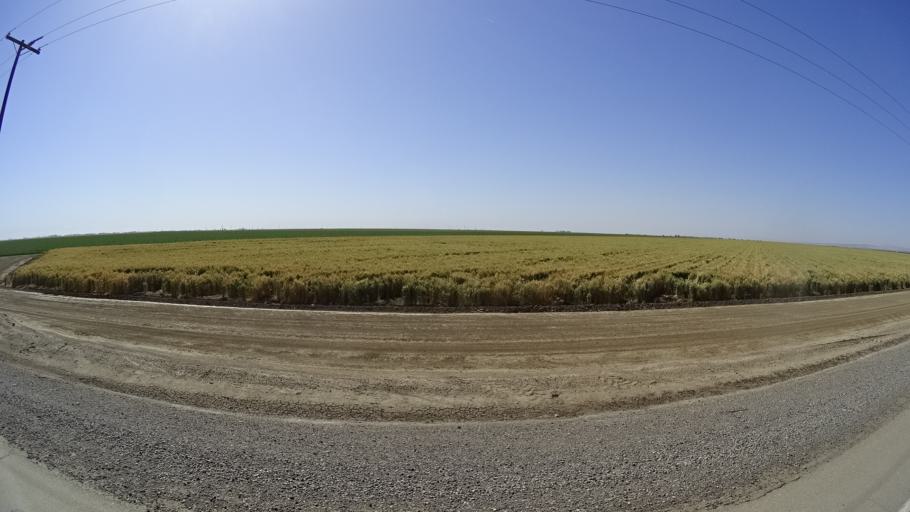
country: US
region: California
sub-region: Kings County
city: Lemoore Station
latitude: 36.1991
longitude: -119.9330
